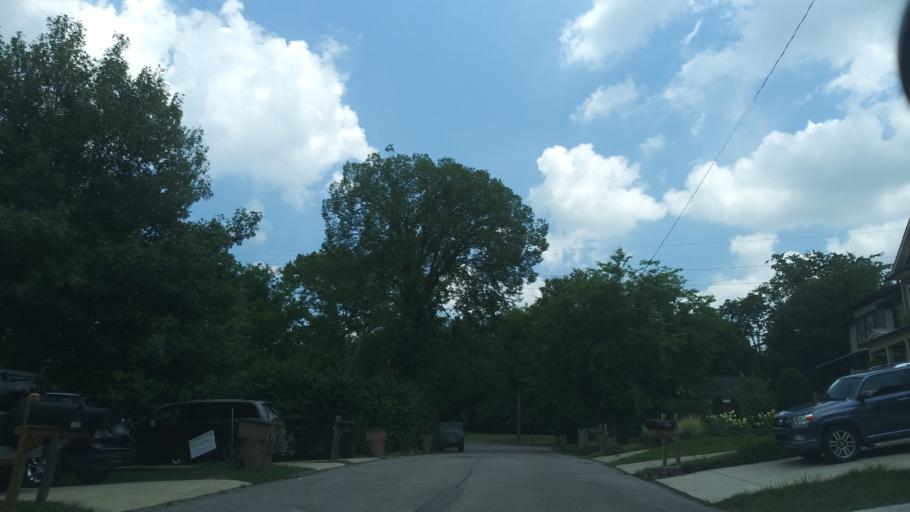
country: US
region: Tennessee
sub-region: Davidson County
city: Nashville
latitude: 36.1425
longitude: -86.8247
